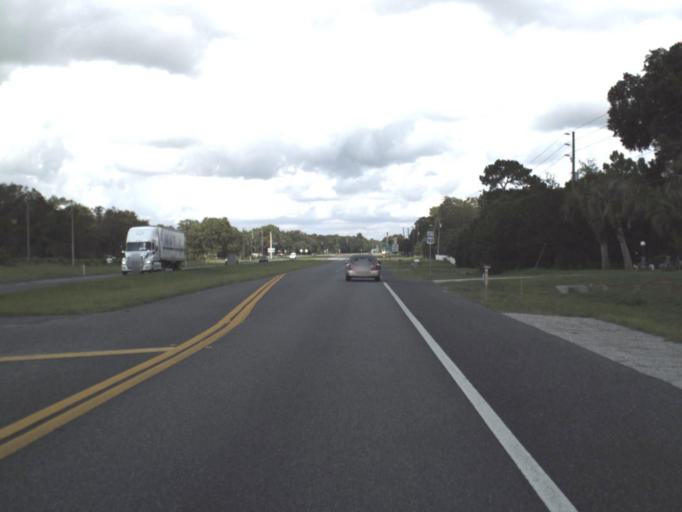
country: US
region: Florida
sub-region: Hernando County
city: Ridge Manor
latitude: 28.5080
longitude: -82.1907
